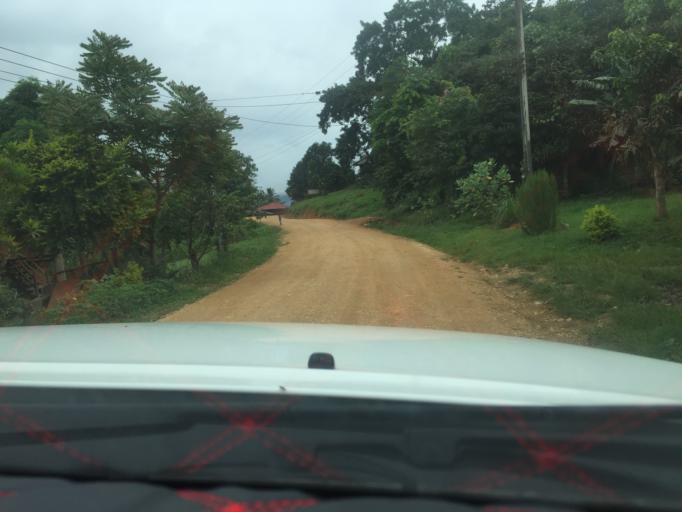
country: TH
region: Phayao
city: Phu Sang
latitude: 19.6862
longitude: 100.5021
